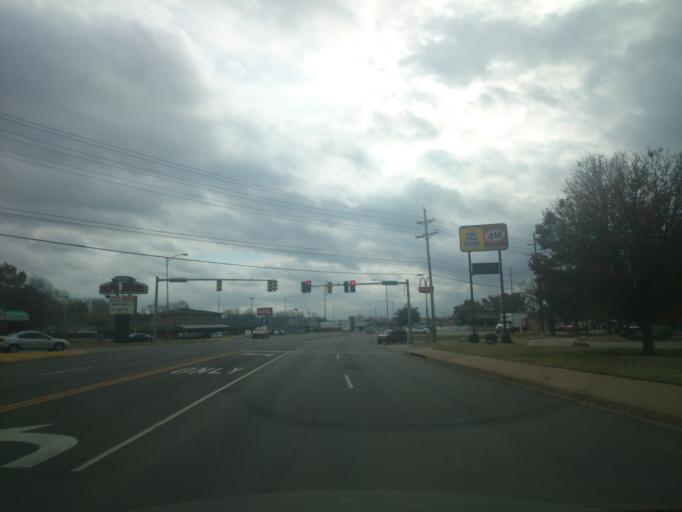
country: US
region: Oklahoma
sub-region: Payne County
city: Stillwater
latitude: 36.1327
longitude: -97.0610
